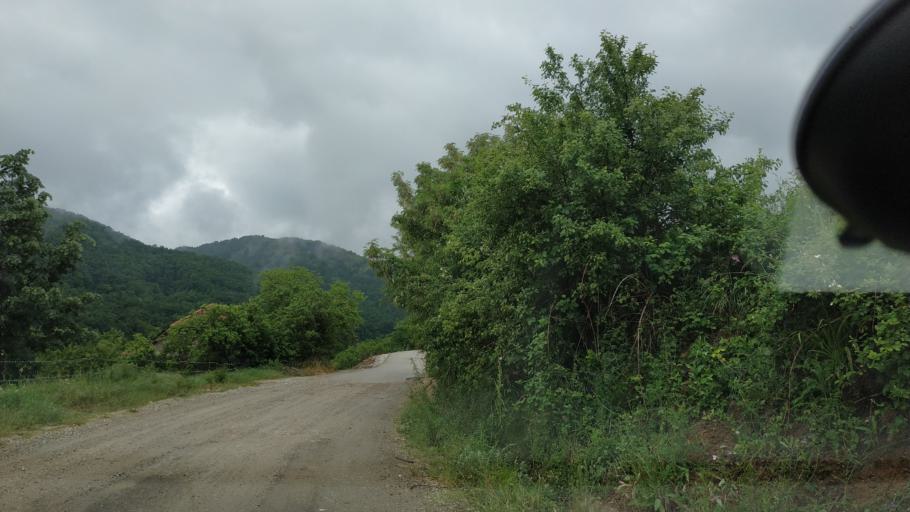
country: RS
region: Central Serbia
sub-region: Toplicki Okrug
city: Prokuplje
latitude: 43.3922
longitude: 21.5730
